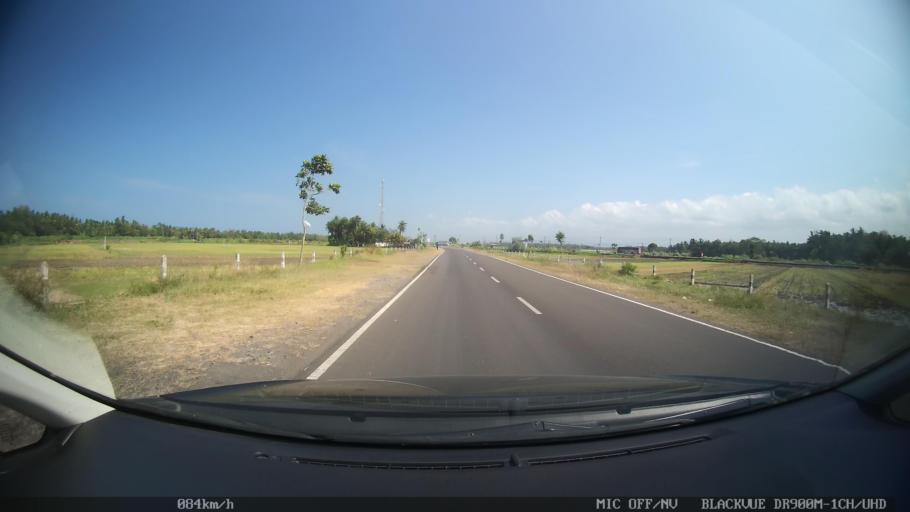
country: ID
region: Daerah Istimewa Yogyakarta
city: Srandakan
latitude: -7.9548
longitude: 110.1962
